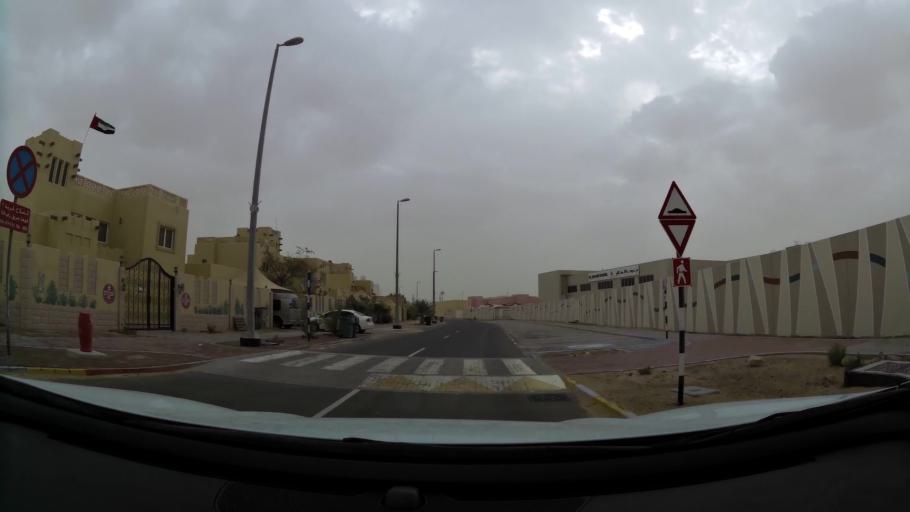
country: AE
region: Abu Dhabi
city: Abu Dhabi
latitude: 24.4475
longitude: 54.7113
